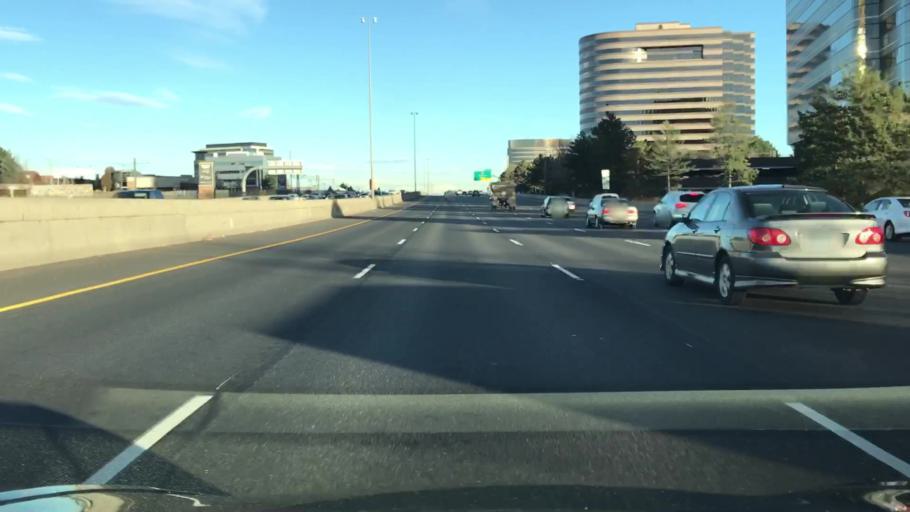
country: US
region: Colorado
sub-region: Arapahoe County
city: Castlewood
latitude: 39.6171
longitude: -104.8979
